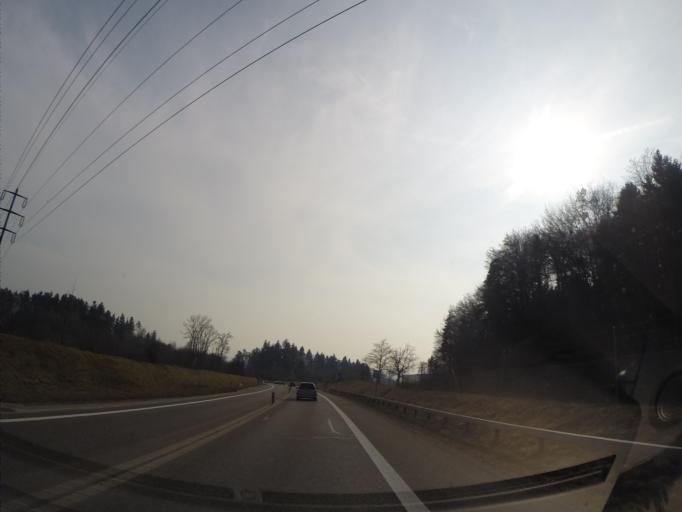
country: CH
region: Zurich
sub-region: Bezirk Andelfingen
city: Henggart
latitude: 47.5530
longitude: 8.6869
